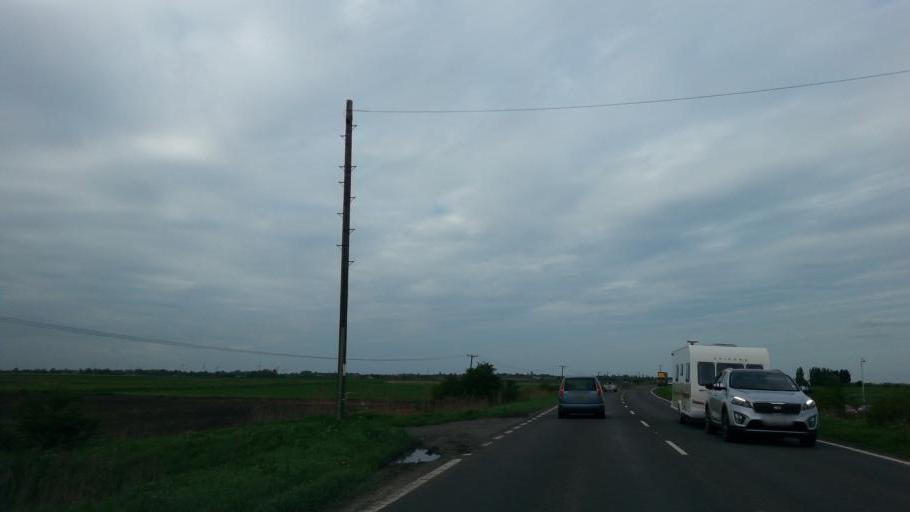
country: GB
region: England
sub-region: Cambridgeshire
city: Chatteris
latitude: 52.4669
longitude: 0.0448
